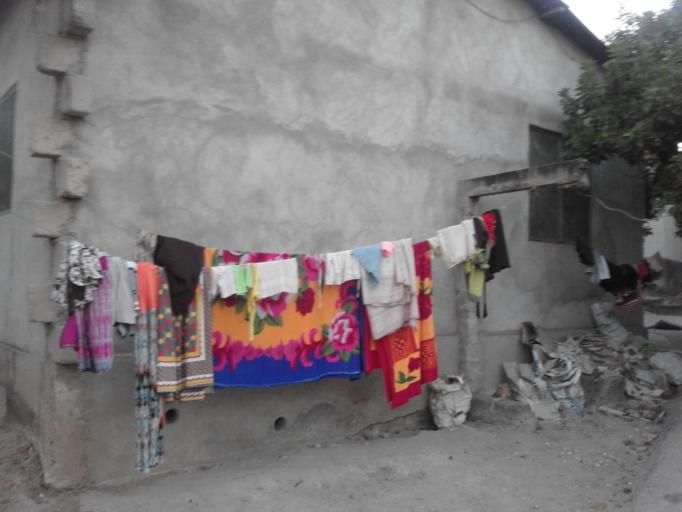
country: TZ
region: Dar es Salaam
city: Magomeni
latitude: -6.7857
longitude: 39.2001
